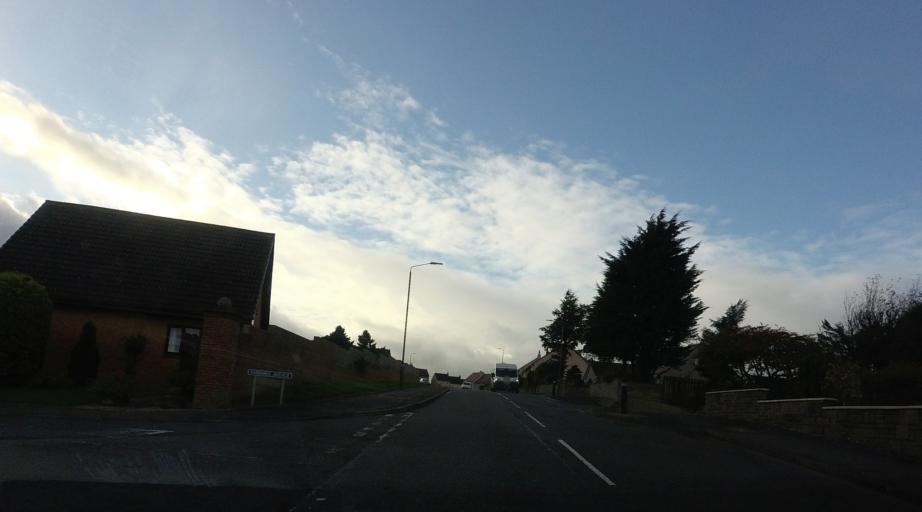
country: GB
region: Scotland
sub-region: Falkirk
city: Polmont
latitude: 55.9731
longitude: -3.7062
